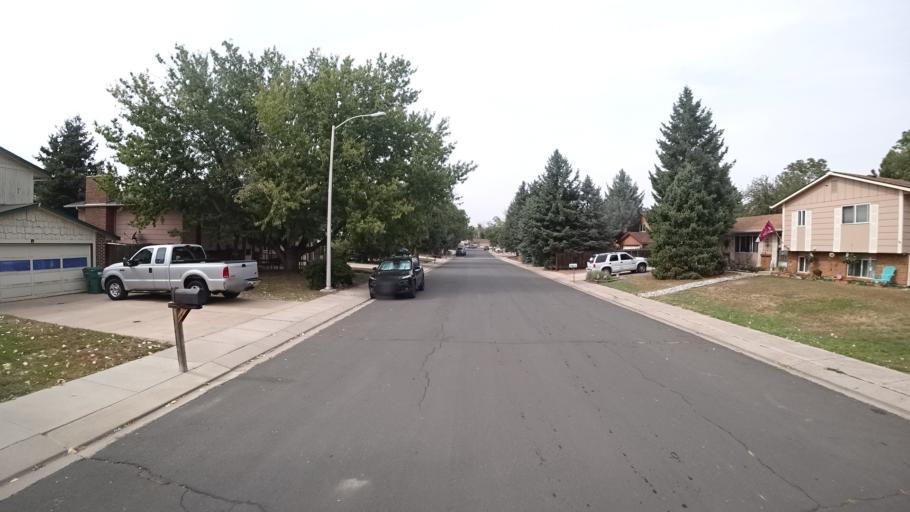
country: US
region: Colorado
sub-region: El Paso County
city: Cimarron Hills
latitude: 38.9008
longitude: -104.7396
